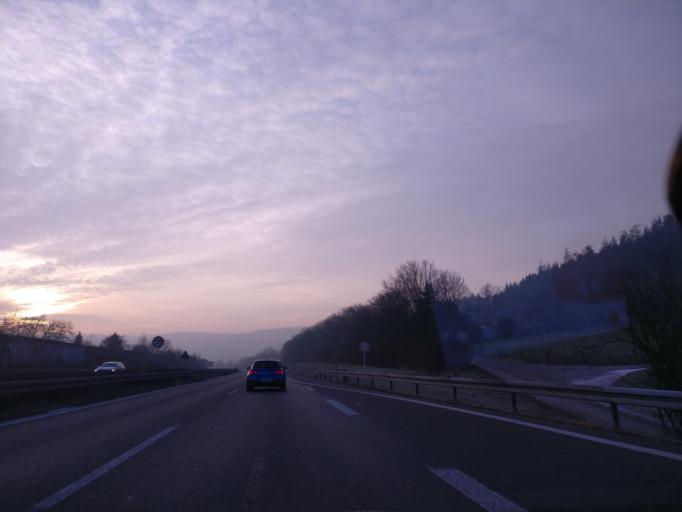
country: DE
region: Baden-Wuerttemberg
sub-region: Regierungsbezirk Stuttgart
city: Pluderhausen
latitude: 48.7901
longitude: 9.5927
